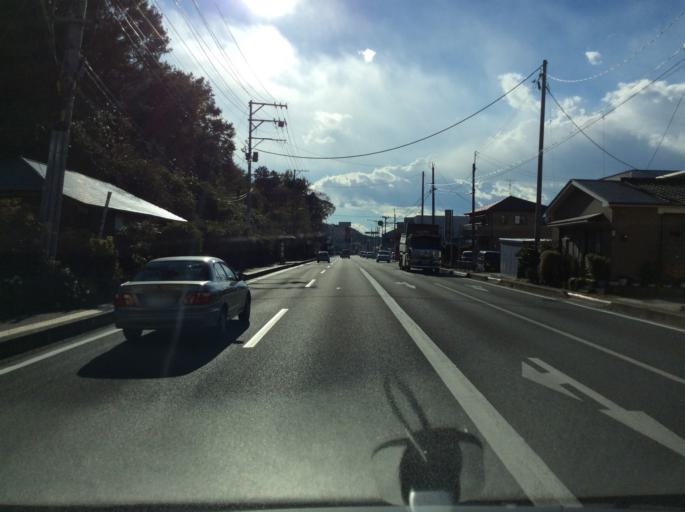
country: JP
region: Fukushima
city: Iwaki
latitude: 37.0460
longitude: 140.8714
